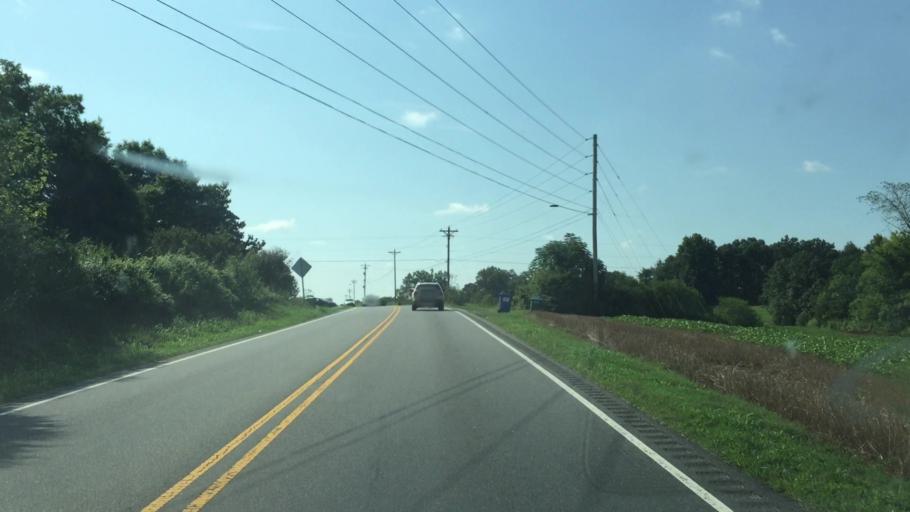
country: US
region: North Carolina
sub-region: Union County
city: Fairview
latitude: 35.1592
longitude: -80.5666
